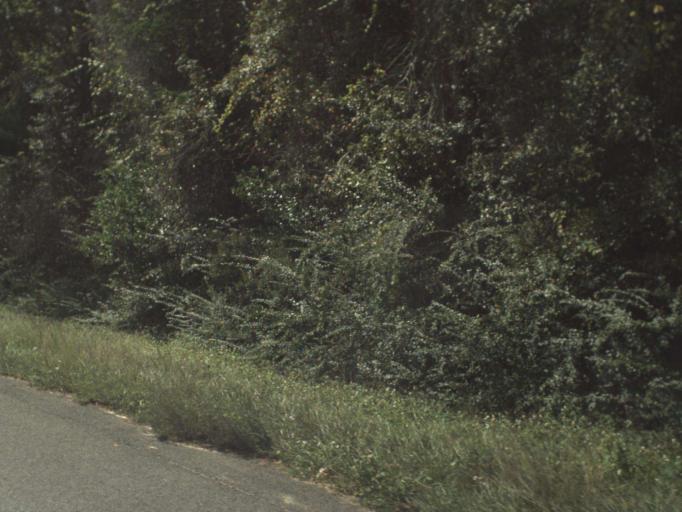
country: US
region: Florida
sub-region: Washington County
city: Chipley
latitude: 30.6267
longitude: -85.5921
